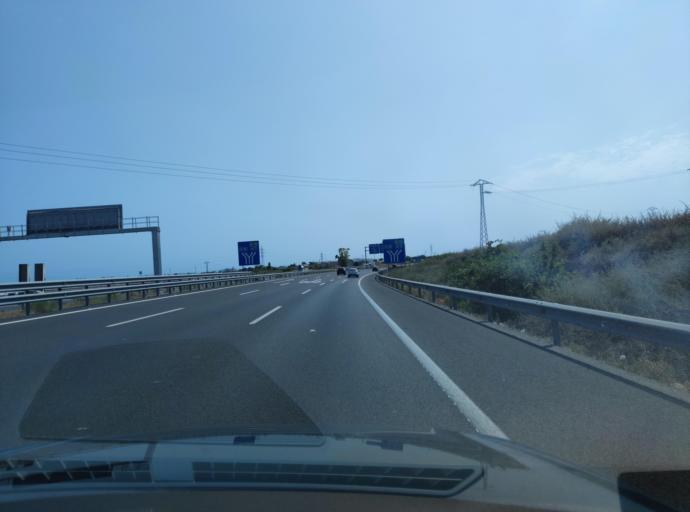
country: ES
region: Valencia
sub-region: Provincia de Valencia
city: Pucol
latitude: 39.6421
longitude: -0.3007
